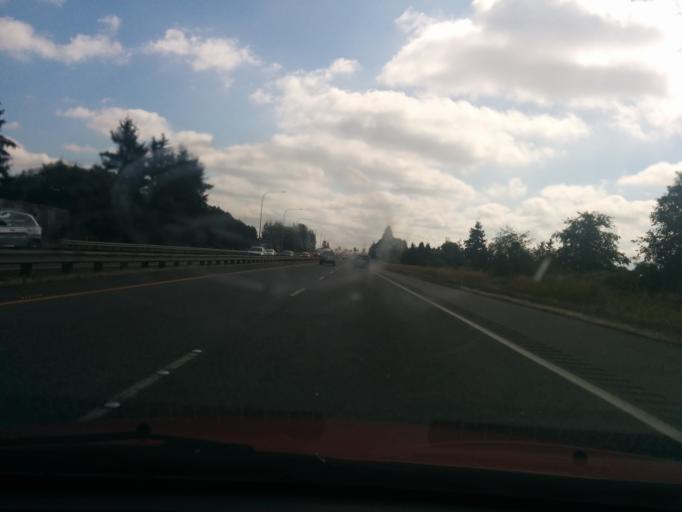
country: US
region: Washington
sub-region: Skagit County
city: Burlington
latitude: 48.4773
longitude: -122.3427
